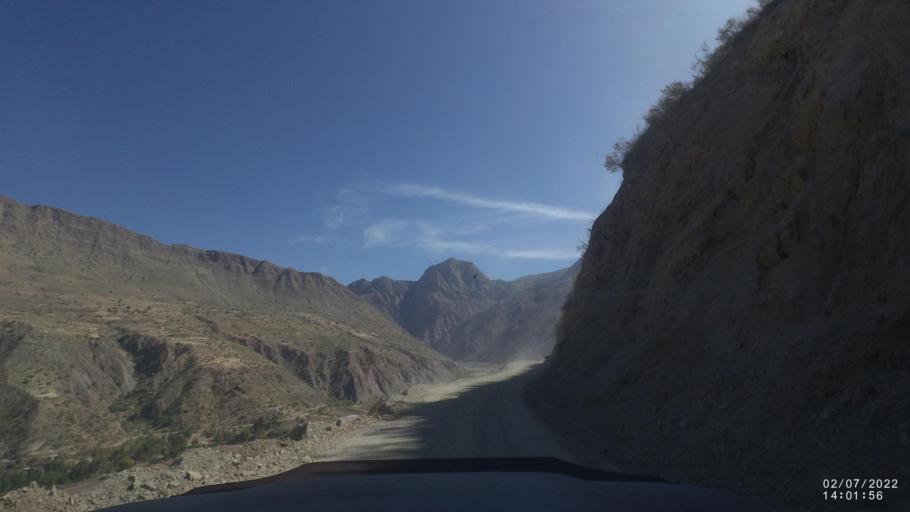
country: BO
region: Cochabamba
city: Irpa Irpa
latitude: -17.8252
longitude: -66.3852
